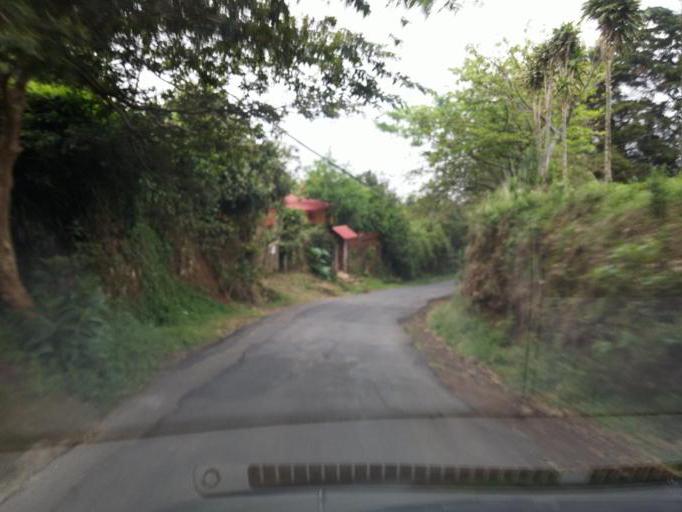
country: CR
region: Heredia
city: San Josecito
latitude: 10.0462
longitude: -84.1050
